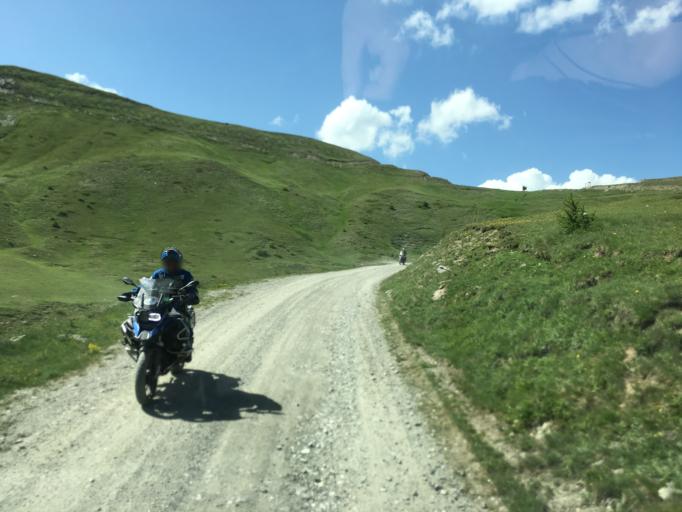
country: IT
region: Piedmont
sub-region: Provincia di Torino
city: Sestriere
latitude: 44.9832
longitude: 6.8714
